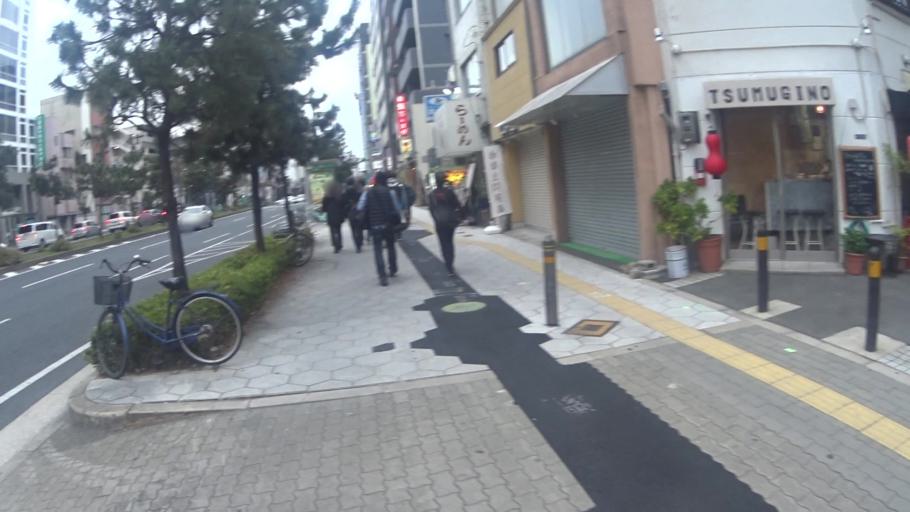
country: JP
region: Osaka
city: Osaka-shi
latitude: 34.6659
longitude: 135.5239
